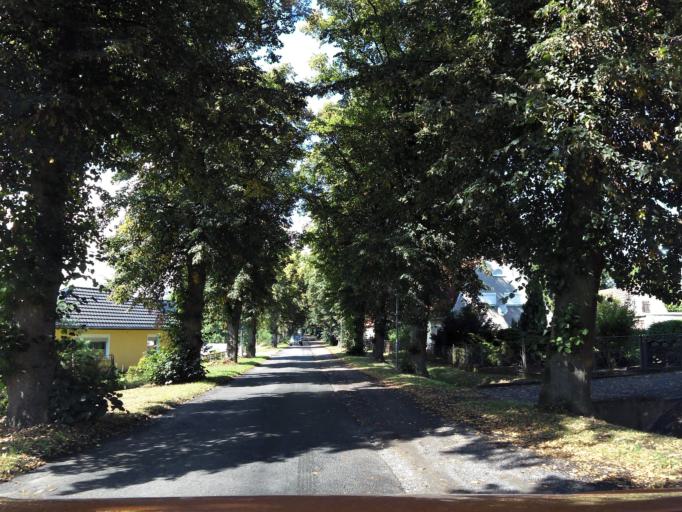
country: DE
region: Brandenburg
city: Ketzin
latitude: 52.4677
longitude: 12.8562
